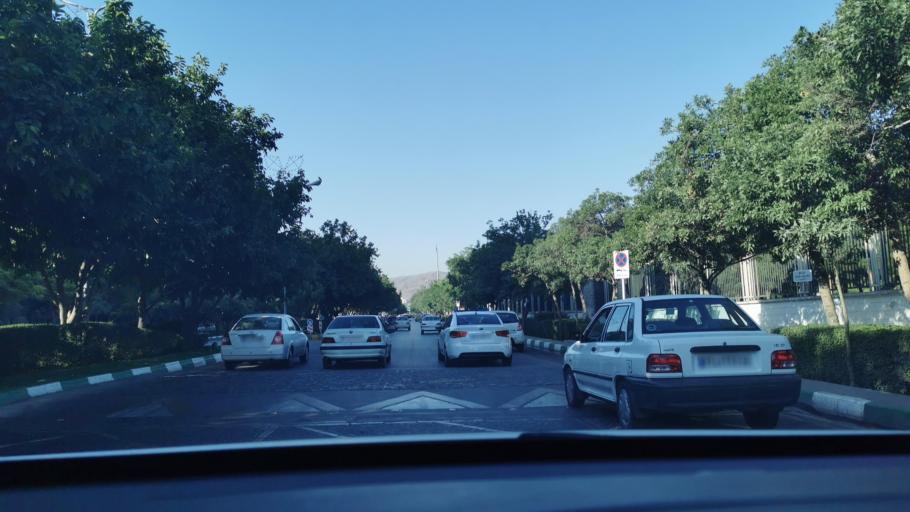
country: IR
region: Razavi Khorasan
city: Mashhad
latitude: 36.2949
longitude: 59.5606
